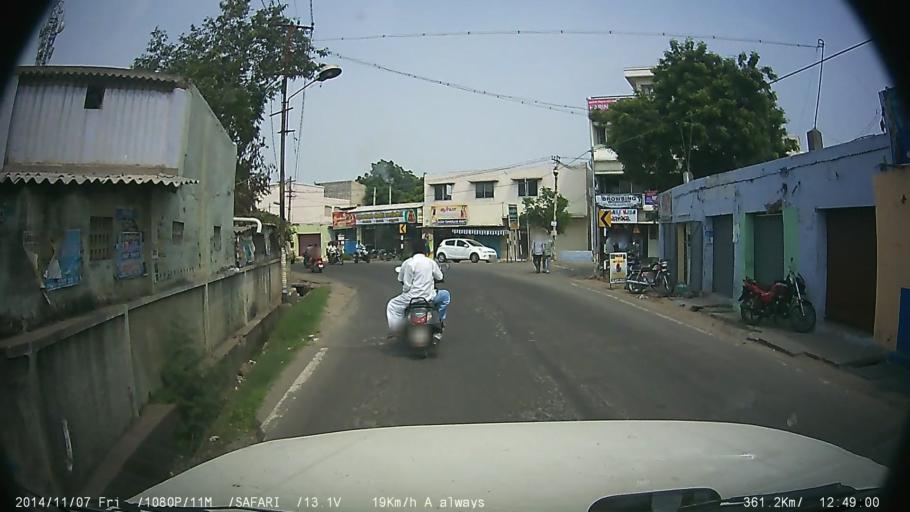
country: IN
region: Tamil Nadu
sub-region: Tiruppur
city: Tiruppur
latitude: 11.0962
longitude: 77.3395
